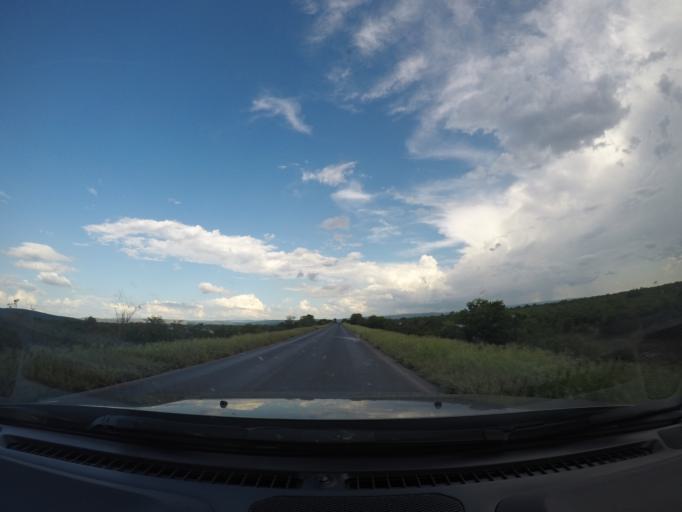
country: BR
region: Bahia
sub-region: Ibotirama
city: Ibotirama
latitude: -12.1607
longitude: -43.2912
